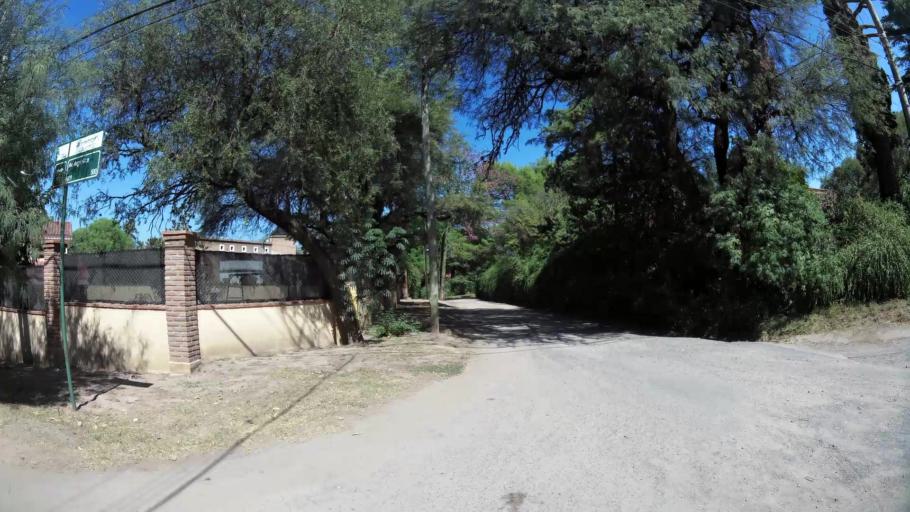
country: AR
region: Cordoba
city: Villa Allende
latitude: -31.2929
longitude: -64.2867
